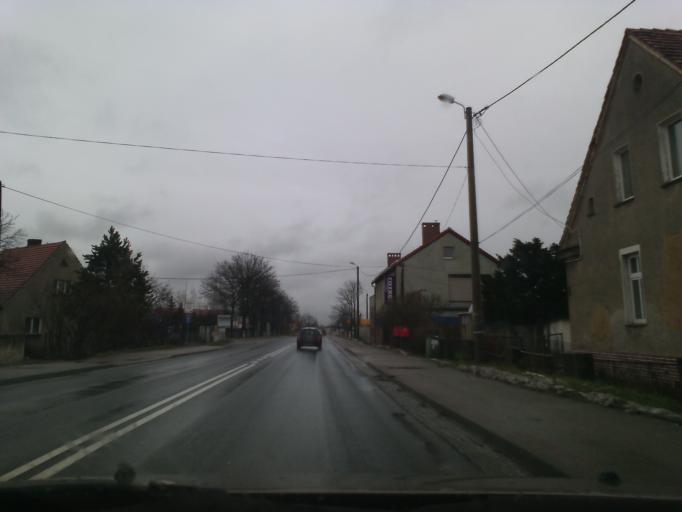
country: PL
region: Lower Silesian Voivodeship
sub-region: Powiat swidnicki
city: Swidnica
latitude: 50.8403
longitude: 16.4384
